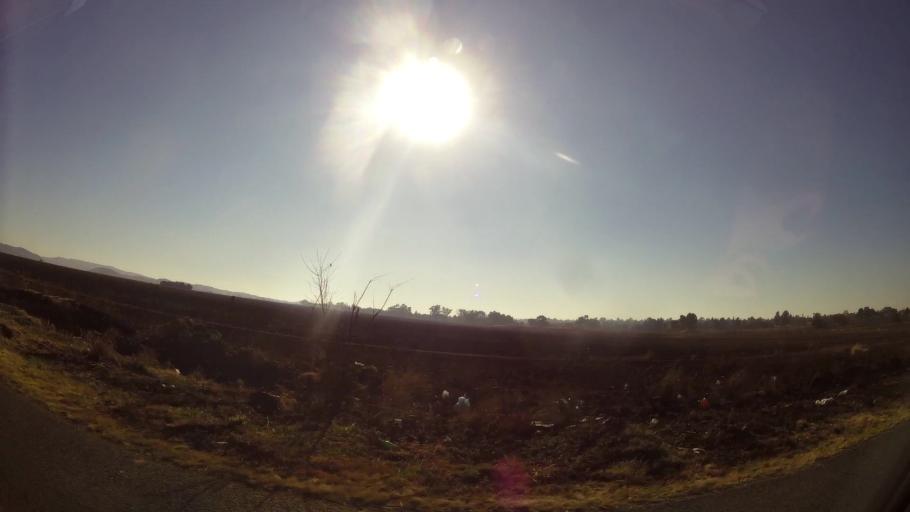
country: ZA
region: Gauteng
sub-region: City of Johannesburg Metropolitan Municipality
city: Johannesburg
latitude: -26.3306
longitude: 28.0751
